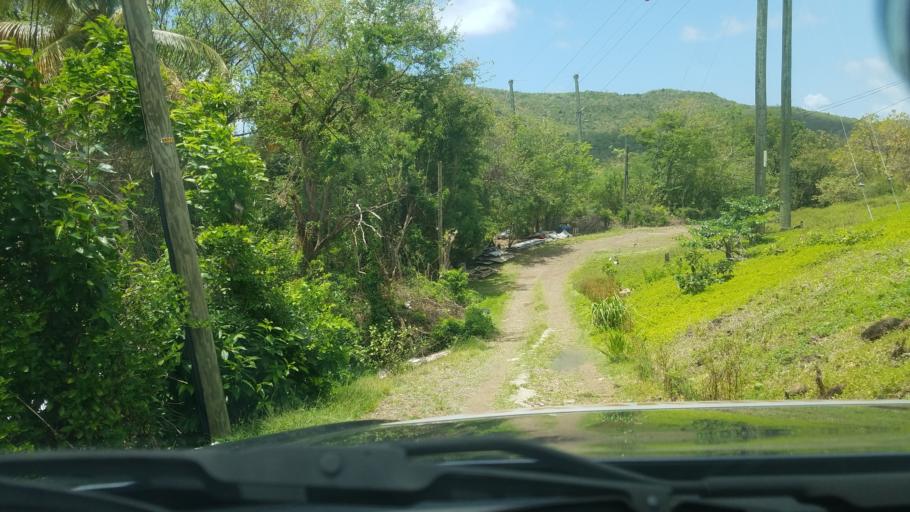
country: LC
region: Gros-Islet
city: Gros Islet
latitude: 14.0542
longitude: -60.9278
